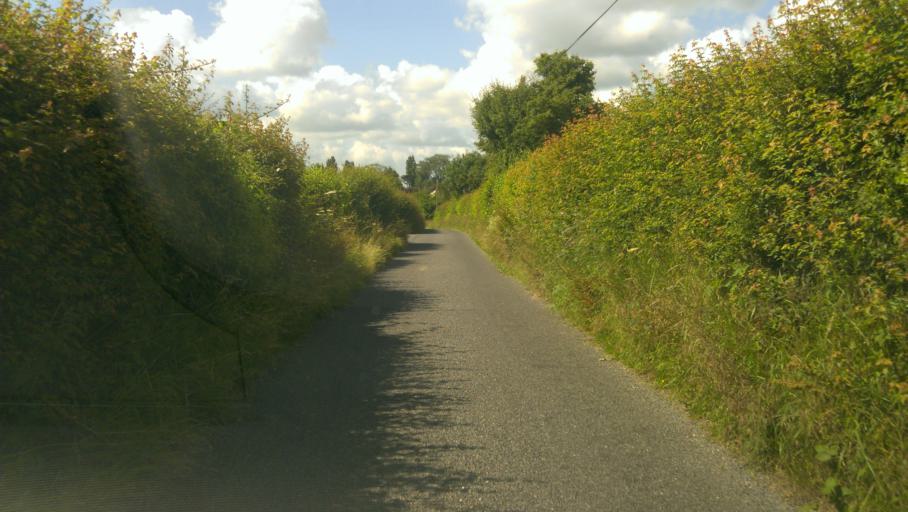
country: GB
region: England
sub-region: Essex
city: Rayne
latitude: 51.8517
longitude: 0.6309
